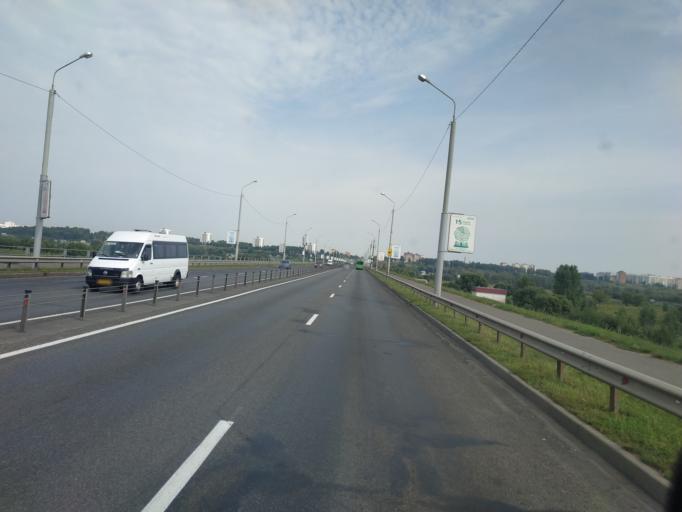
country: BY
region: Mogilev
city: Mahilyow
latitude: 53.8881
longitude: 30.3774
